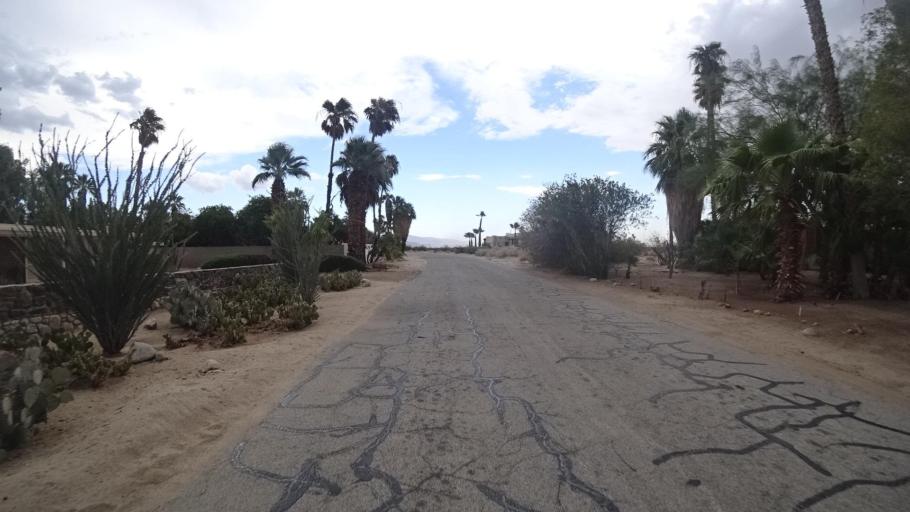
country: US
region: California
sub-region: San Diego County
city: Borrego Springs
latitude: 33.2850
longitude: -116.3885
